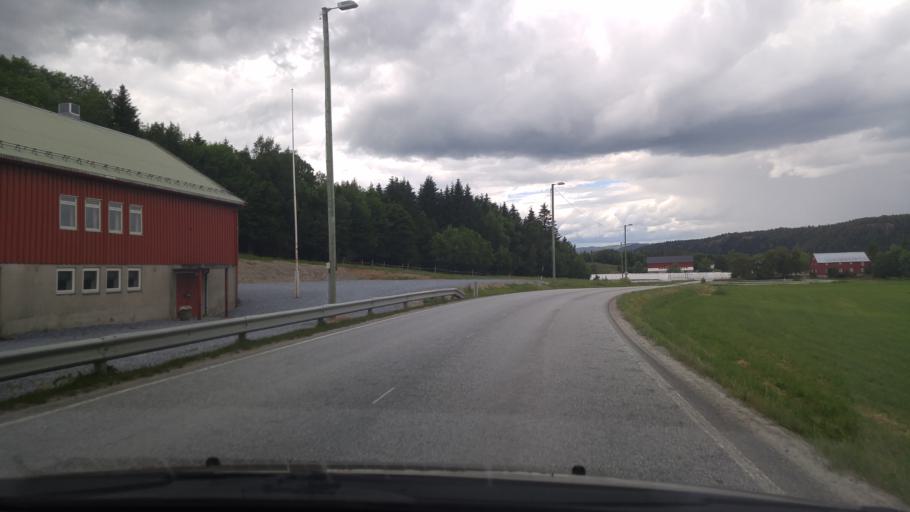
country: NO
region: Nord-Trondelag
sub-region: Steinkjer
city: Steinkjer
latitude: 64.0967
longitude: 11.4440
